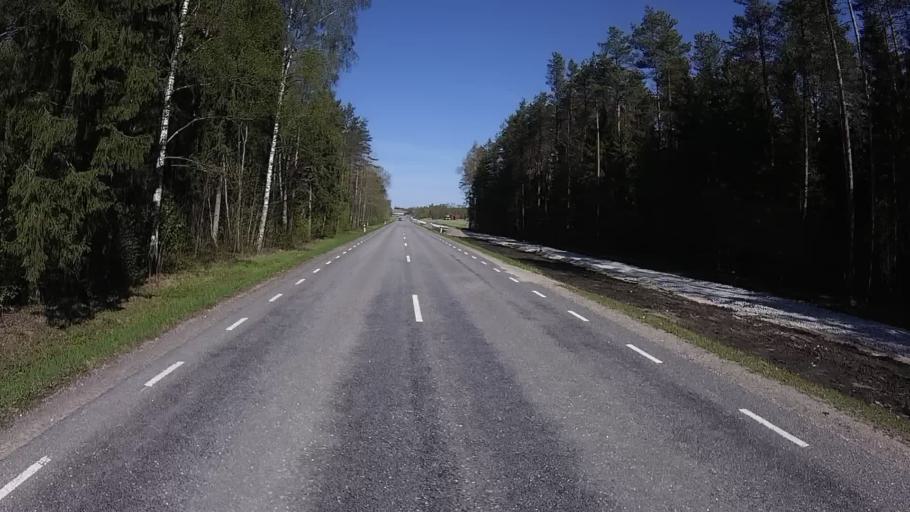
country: EE
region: Paernumaa
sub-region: Tootsi vald
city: Tootsi
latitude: 58.4968
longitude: 24.8035
